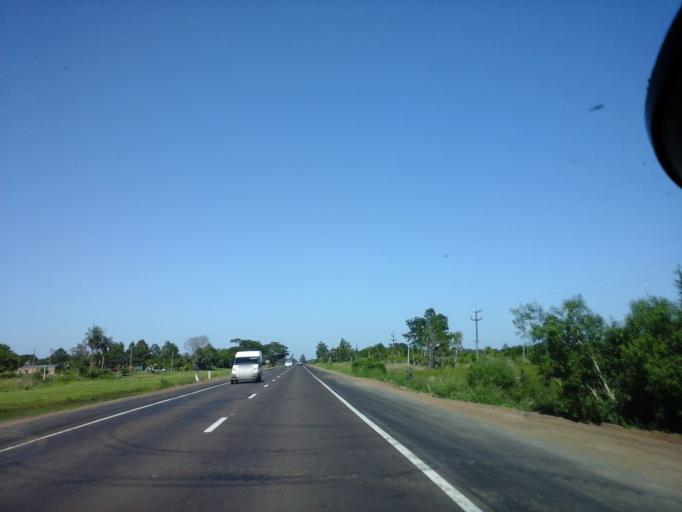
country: AR
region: Corrientes
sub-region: Departamento de Itati
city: Itati
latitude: -27.3669
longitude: -58.3462
